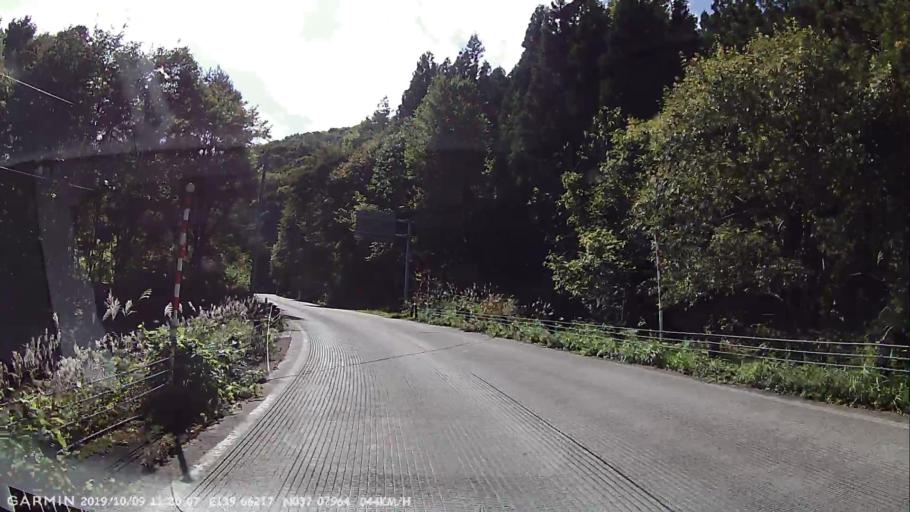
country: JP
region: Tochigi
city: Nikko
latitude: 37.0797
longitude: 139.6623
